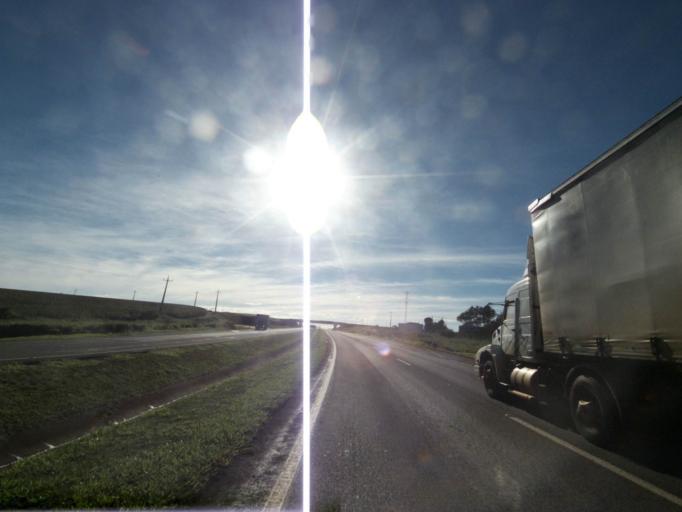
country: BR
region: Parana
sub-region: Cascavel
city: Cascavel
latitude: -25.0266
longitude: -53.5540
